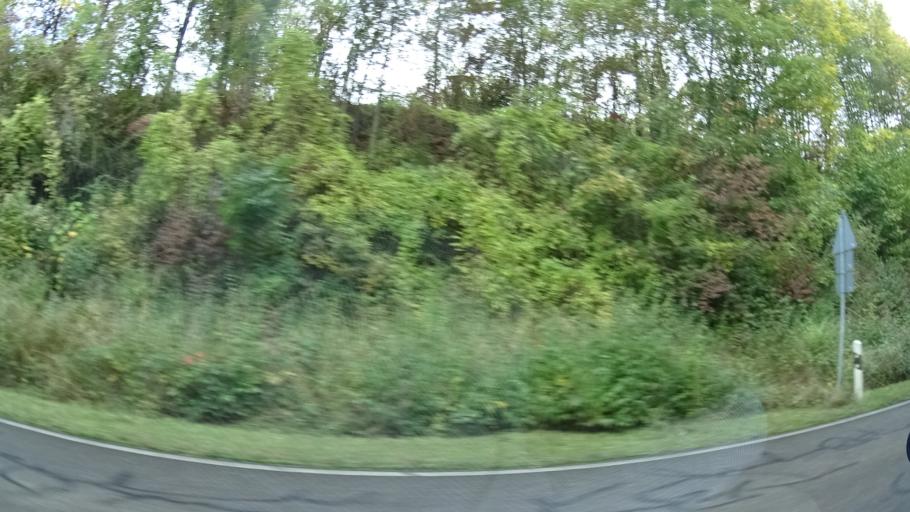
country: DE
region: Baden-Wuerttemberg
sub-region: Karlsruhe Region
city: Ostringen
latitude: 49.1976
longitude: 8.6895
